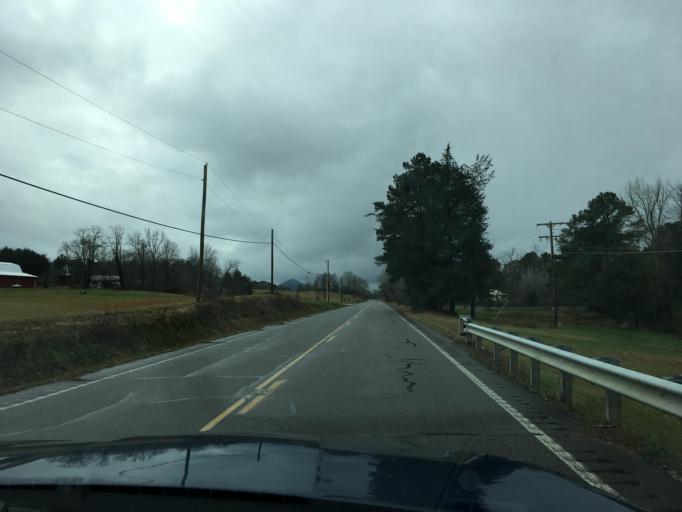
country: US
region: Tennessee
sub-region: Polk County
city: Benton
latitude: 35.1444
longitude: -84.6427
